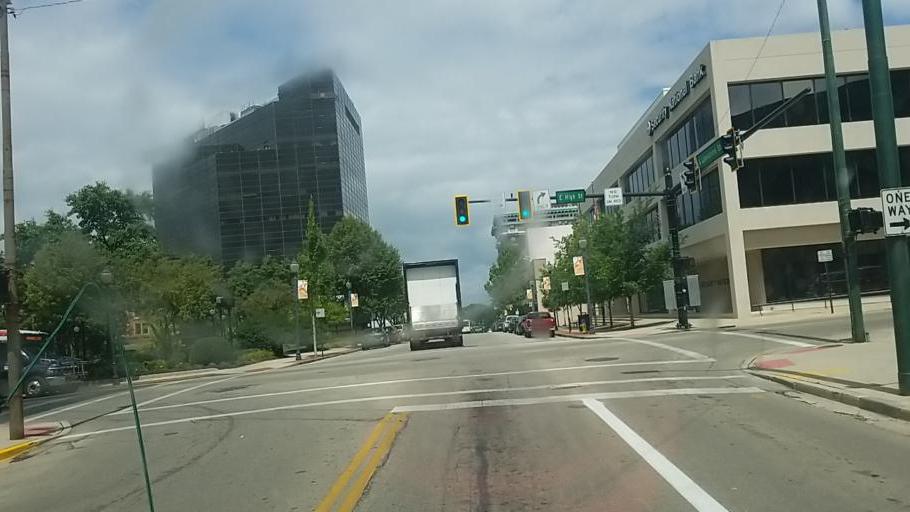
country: US
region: Ohio
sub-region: Clark County
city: Springfield
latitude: 39.9230
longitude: -83.8086
